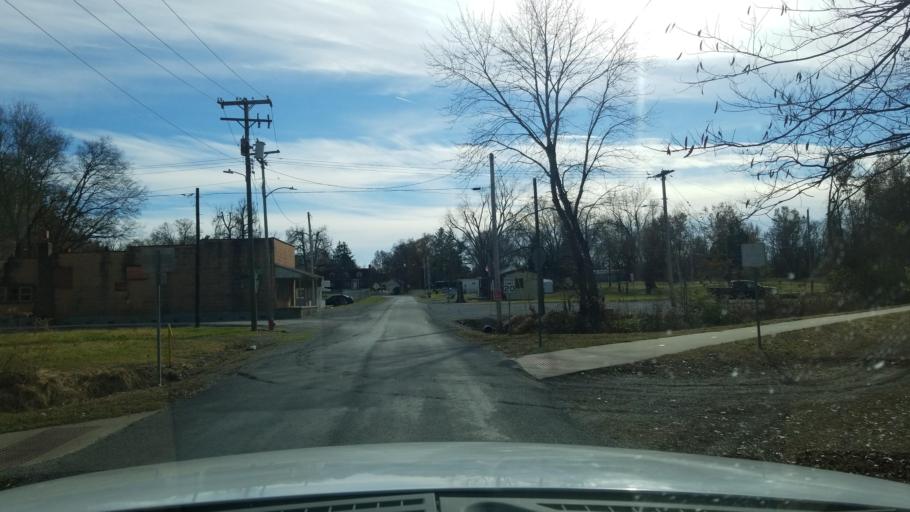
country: US
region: Illinois
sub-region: Saline County
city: Harrisburg
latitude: 37.7656
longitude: -88.5171
